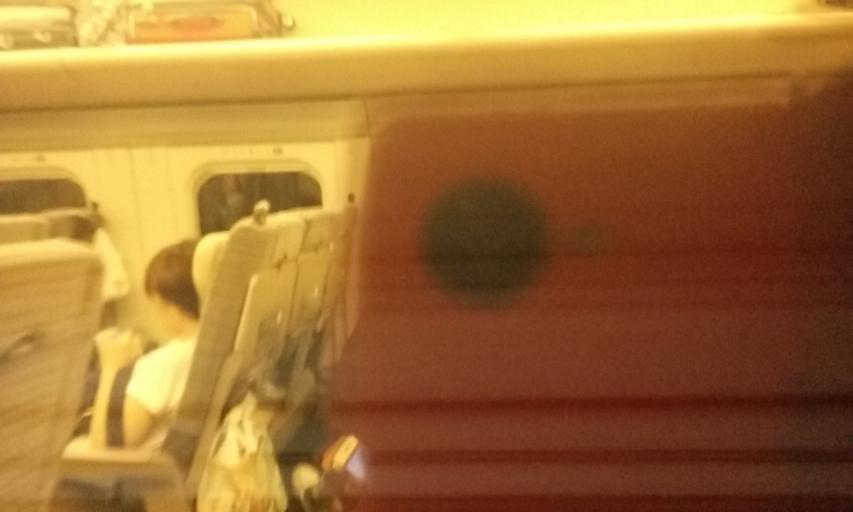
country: JP
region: Tochigi
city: Kuroiso
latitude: 36.9849
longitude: 140.0726
